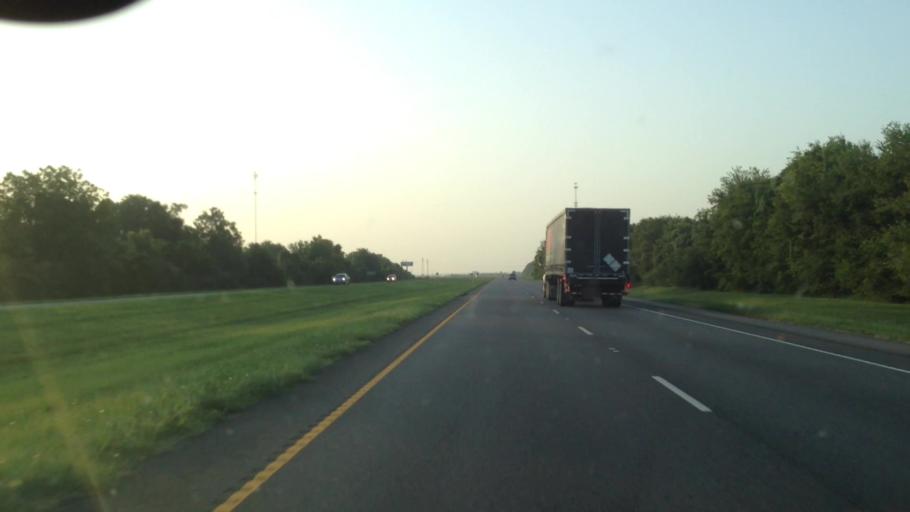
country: US
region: Louisiana
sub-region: Red River Parish
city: Coushatta
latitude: 31.8468
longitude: -93.2952
